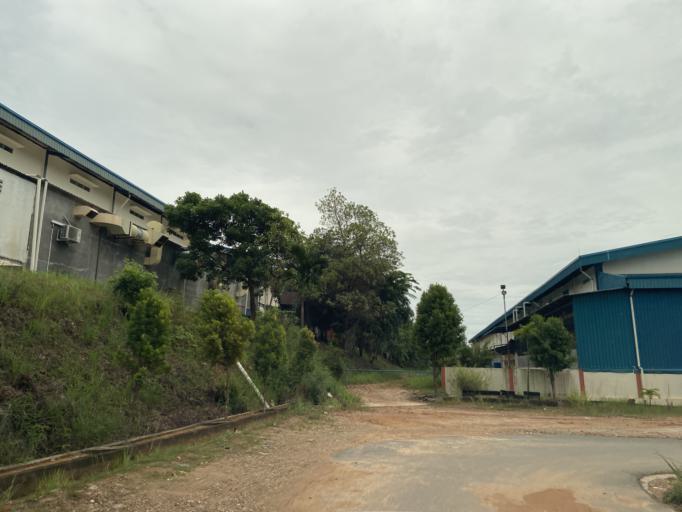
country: SG
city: Singapore
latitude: 1.1665
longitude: 104.0196
